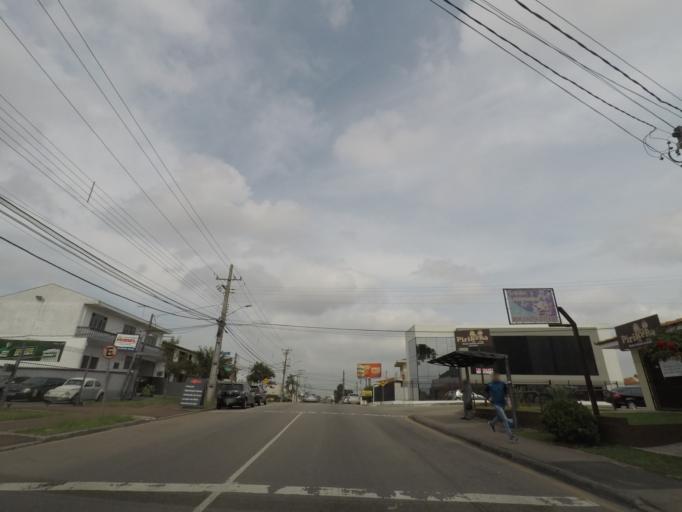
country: BR
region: Parana
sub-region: Curitiba
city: Curitiba
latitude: -25.4958
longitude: -49.2870
